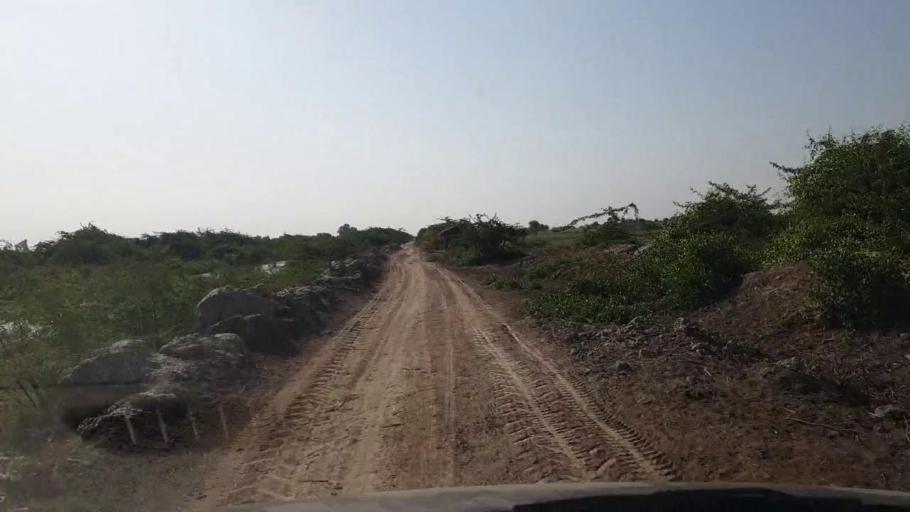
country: PK
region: Sindh
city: Kadhan
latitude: 24.6023
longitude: 69.0744
